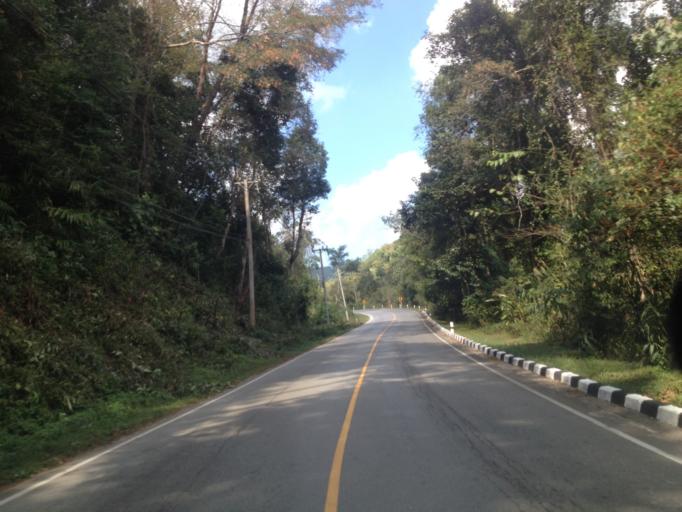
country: TH
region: Mae Hong Son
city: Ban Huai I Huak
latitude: 18.1492
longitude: 98.1425
